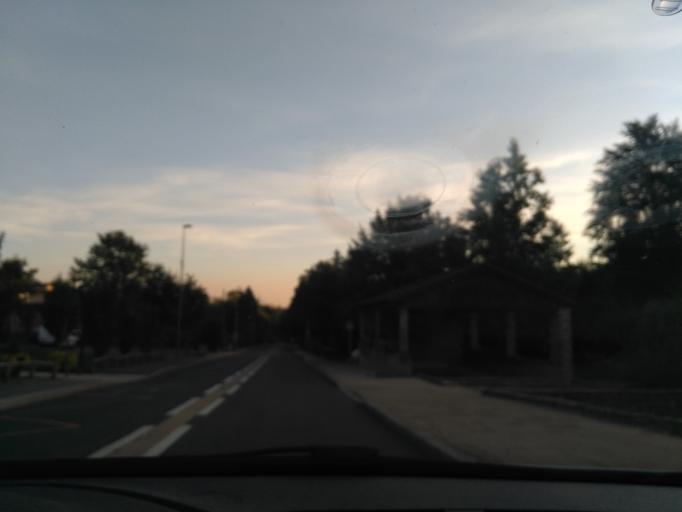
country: FR
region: Rhone-Alpes
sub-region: Departement du Rhone
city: Albigny-sur-Saone
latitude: 45.8702
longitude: 4.8205
